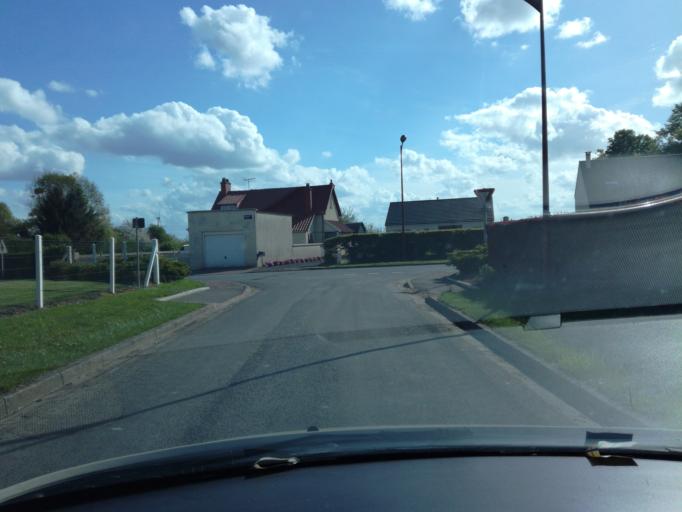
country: FR
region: Picardie
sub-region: Departement de la Somme
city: Hornoy-le-Bourg
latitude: 49.8282
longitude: 1.9357
